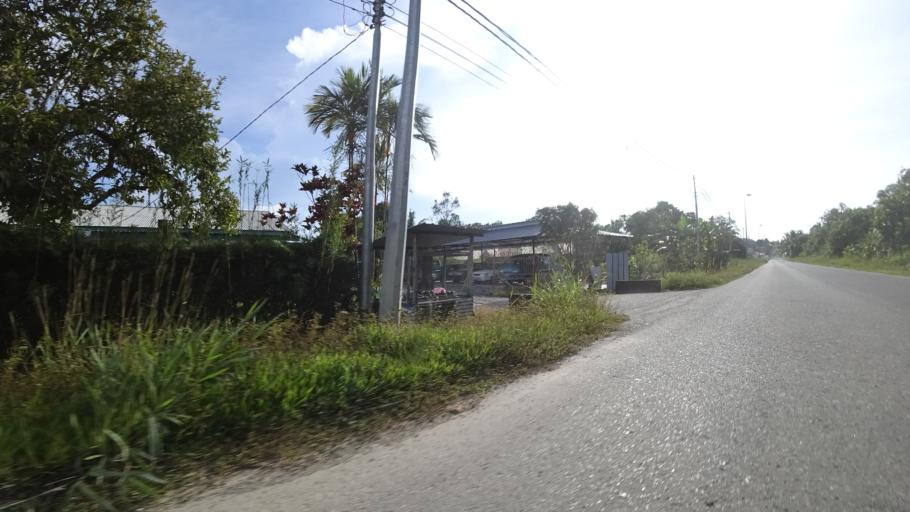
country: BN
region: Brunei and Muara
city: Bandar Seri Begawan
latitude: 4.8432
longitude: 114.8464
